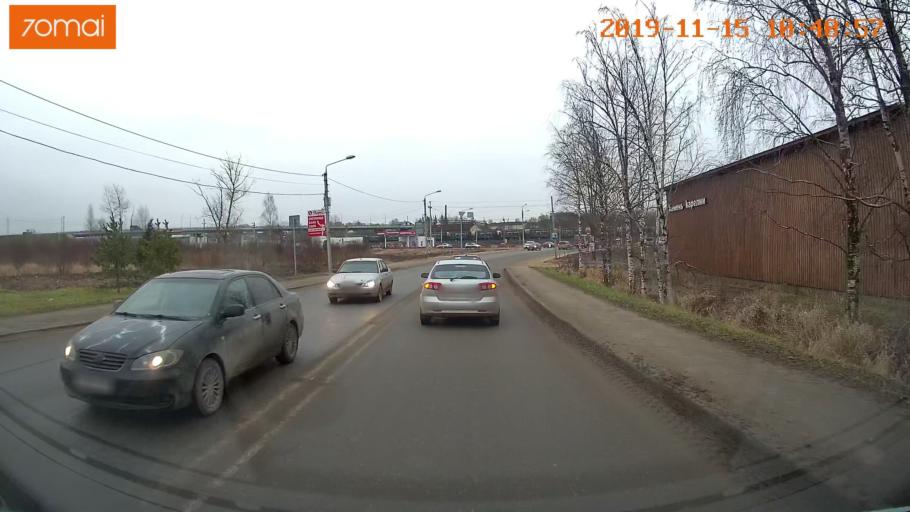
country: RU
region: Vologda
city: Sheksna
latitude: 59.2117
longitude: 38.5114
